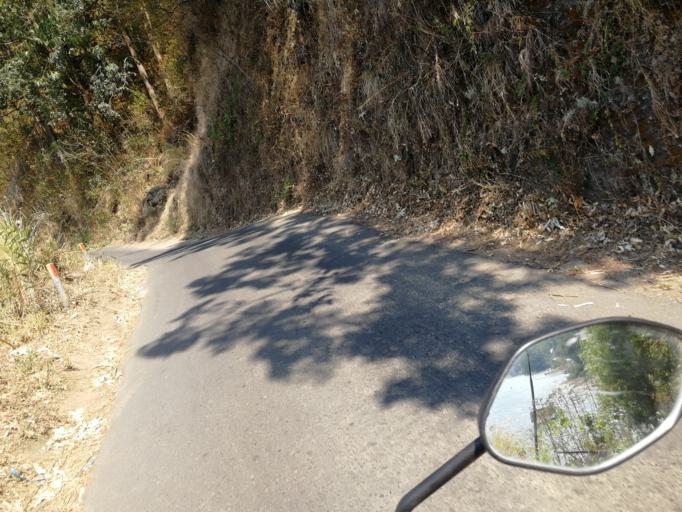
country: ID
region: Bali
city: Banjar Buahan
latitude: -8.2857
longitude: 115.4008
